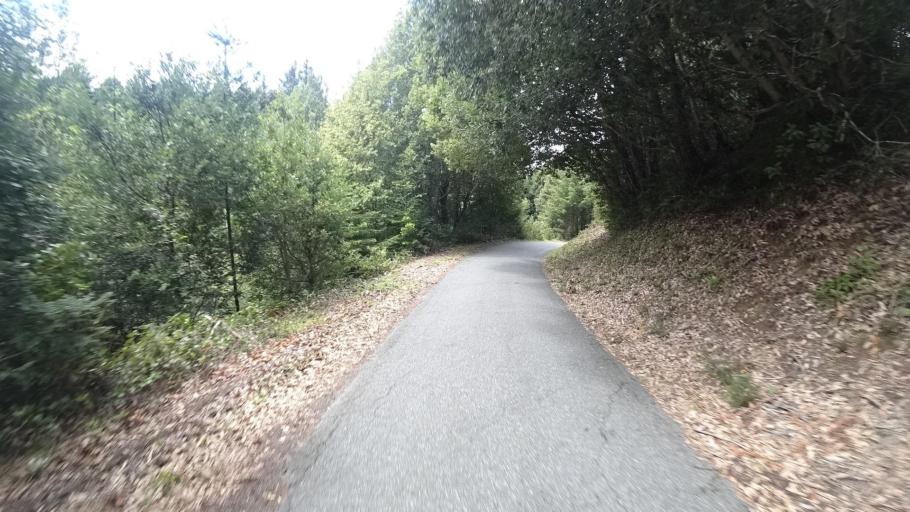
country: US
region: California
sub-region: Humboldt County
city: Blue Lake
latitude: 40.7928
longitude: -123.9734
